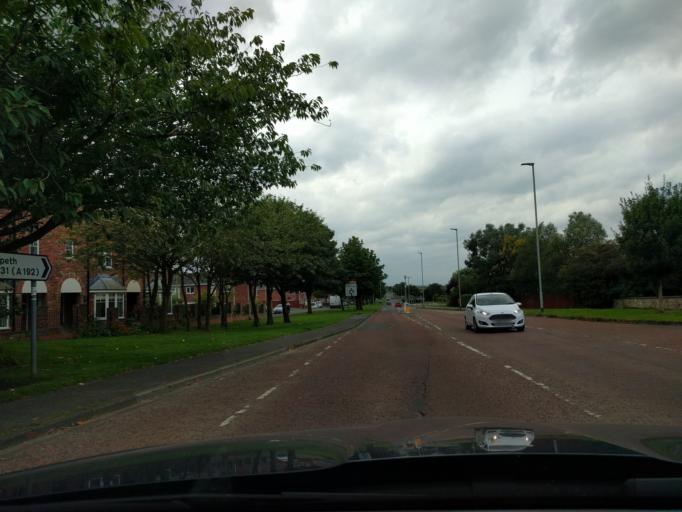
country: GB
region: England
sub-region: Northumberland
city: Bedlington
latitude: 55.1332
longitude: -1.6083
